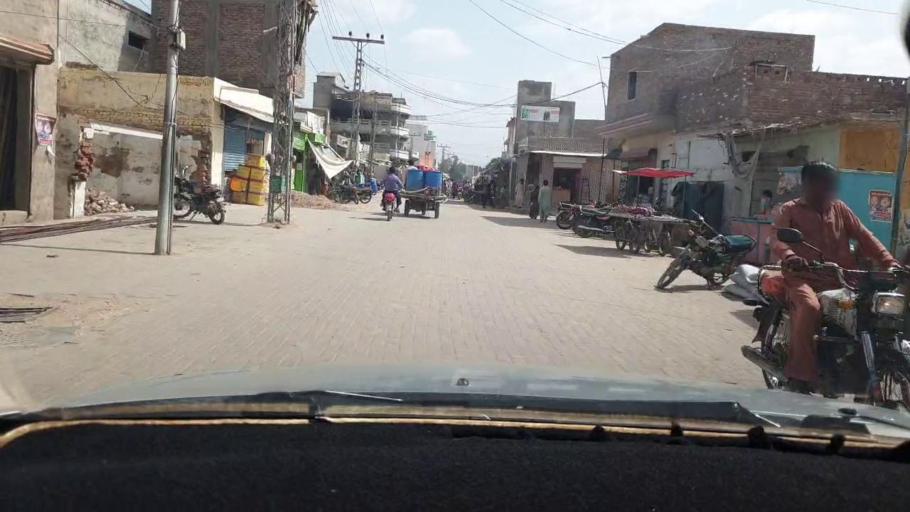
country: PK
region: Sindh
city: Digri
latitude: 25.0725
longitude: 69.2158
